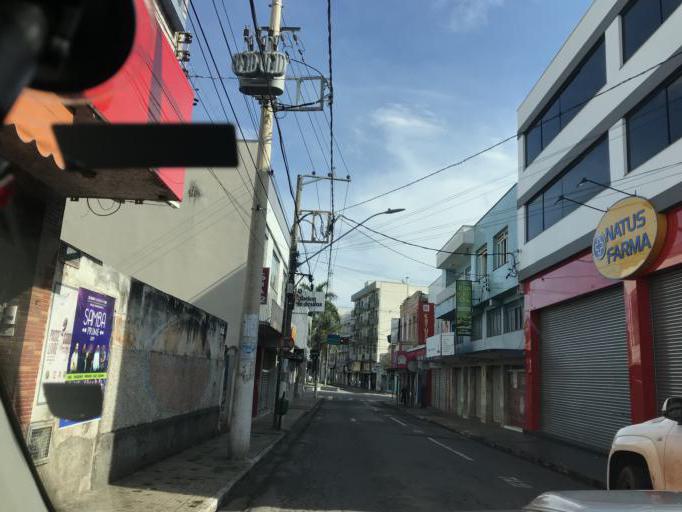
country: BR
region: Minas Gerais
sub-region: Tres Coracoes
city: Tres Coracoes
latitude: -21.6982
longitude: -45.2562
